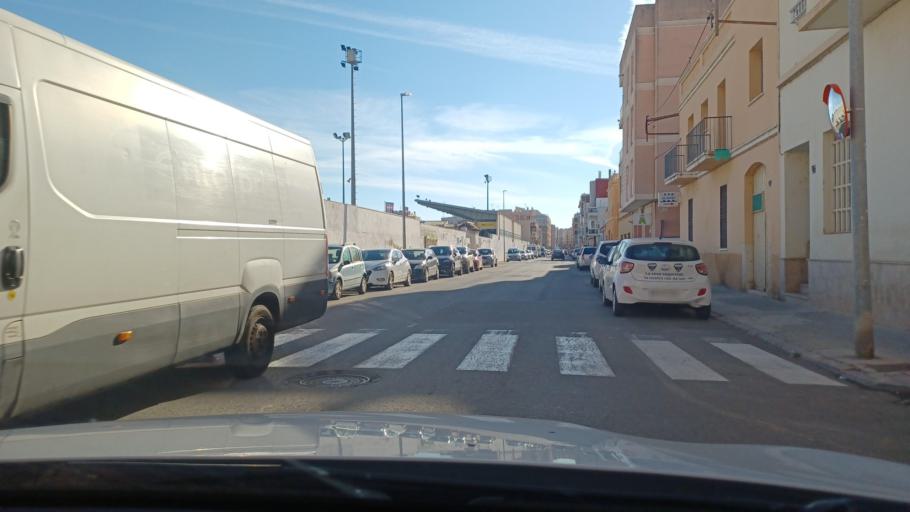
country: ES
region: Catalonia
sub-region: Provincia de Tarragona
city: Amposta
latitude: 40.7085
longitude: 0.5807
